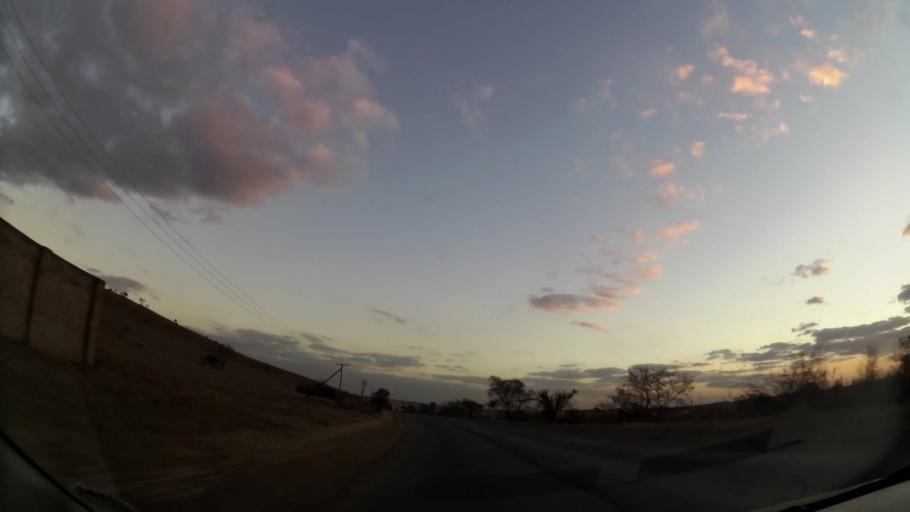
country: ZA
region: Gauteng
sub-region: West Rand District Municipality
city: Krugersdorp
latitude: -26.0356
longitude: 27.7245
